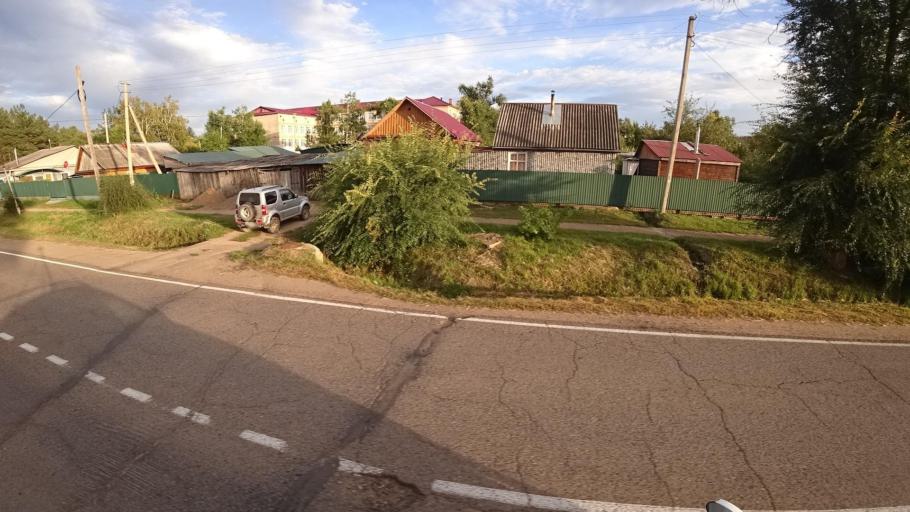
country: RU
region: Primorskiy
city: Yakovlevka
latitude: 44.4261
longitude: 133.4722
